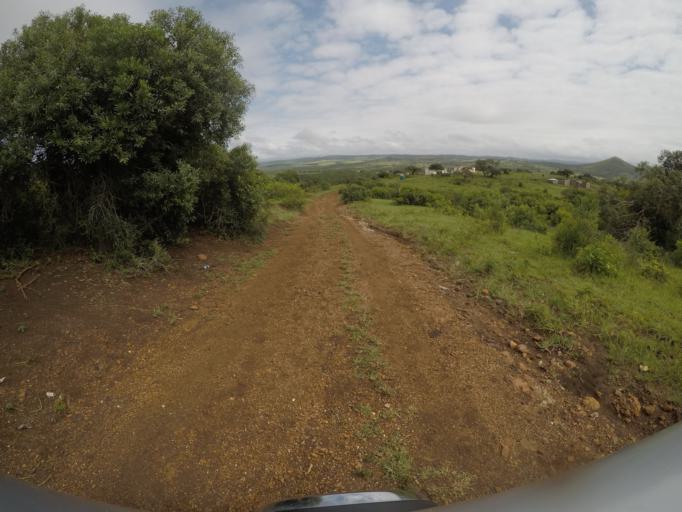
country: ZA
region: KwaZulu-Natal
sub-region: uThungulu District Municipality
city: Empangeni
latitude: -28.6288
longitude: 31.8647
